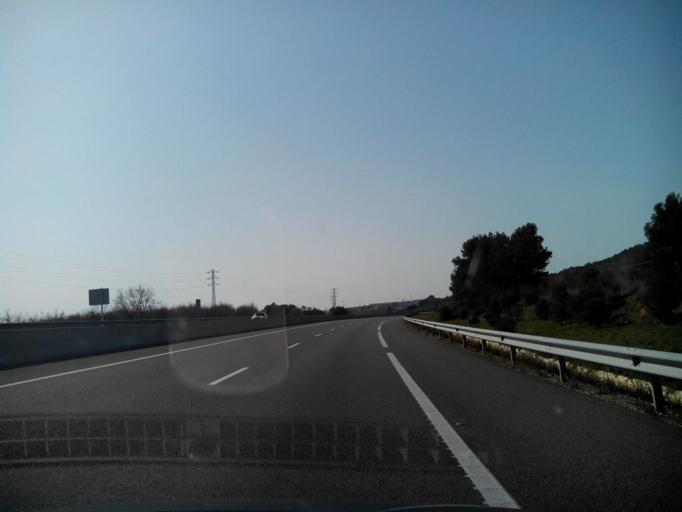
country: ES
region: Catalonia
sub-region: Provincia de Tarragona
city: Alcover
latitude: 41.2476
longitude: 1.1718
